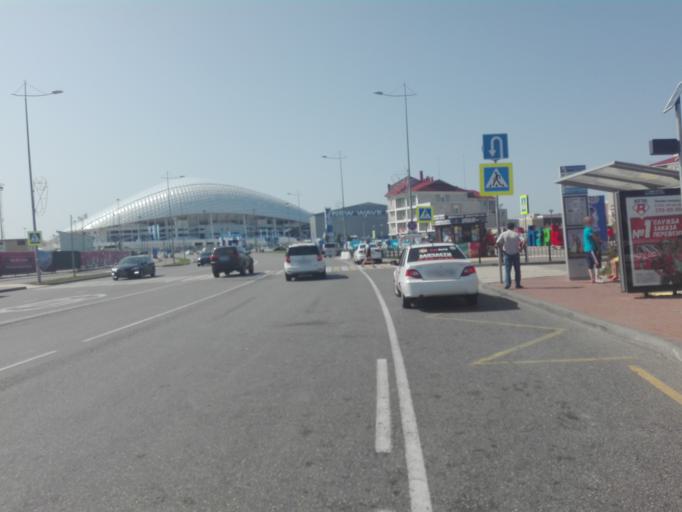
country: RU
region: Krasnodarskiy
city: Adler
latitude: 43.4024
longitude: 39.9633
